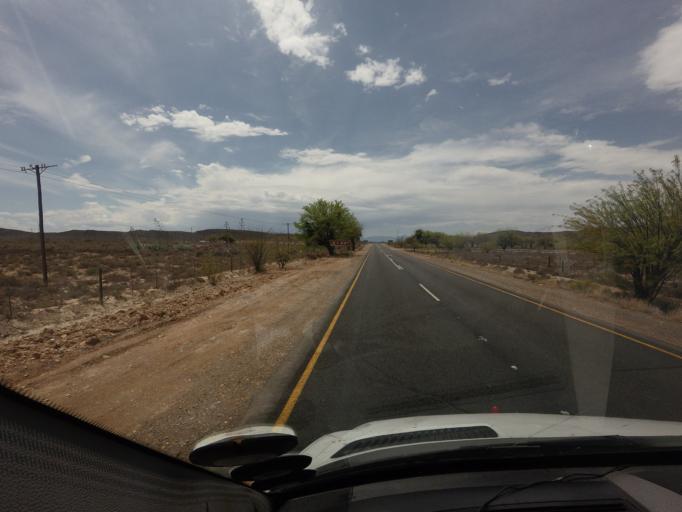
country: ZA
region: Western Cape
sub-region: Eden District Municipality
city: Ladismith
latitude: -33.7762
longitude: 20.9339
